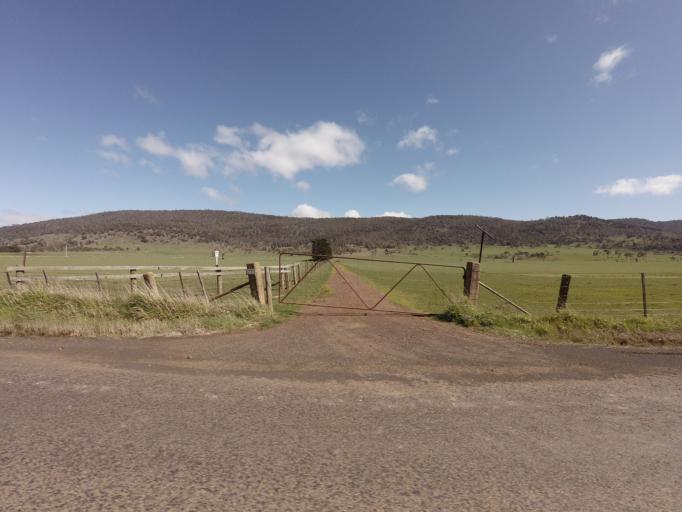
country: AU
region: Tasmania
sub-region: Northern Midlands
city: Evandale
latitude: -41.9619
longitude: 147.4390
